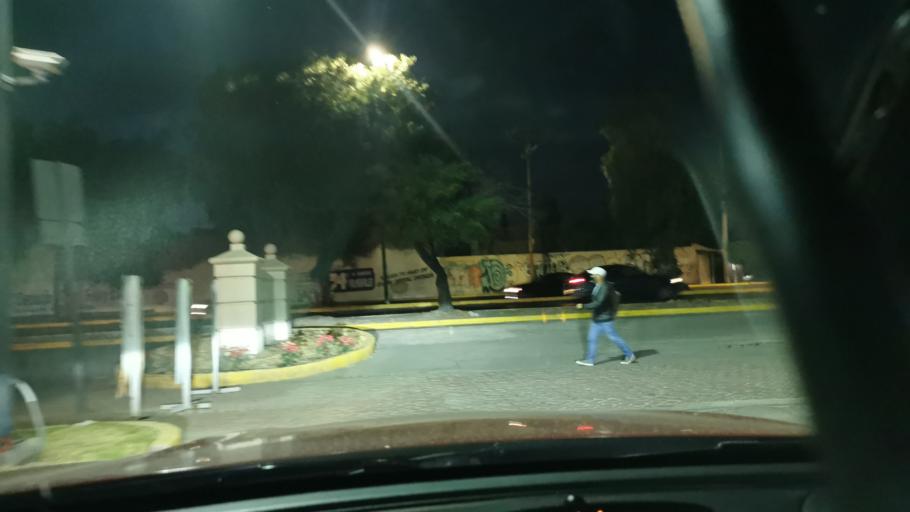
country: MX
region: Mexico
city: Cuautitlan Izcalli
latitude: 19.6465
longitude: -99.2174
